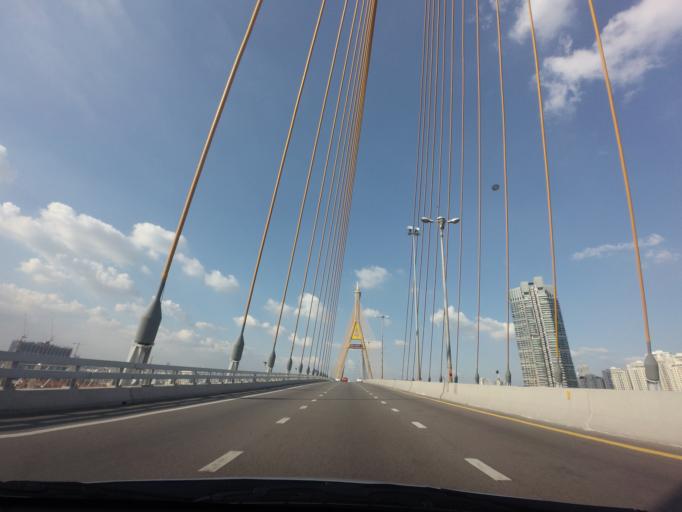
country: TH
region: Samut Prakan
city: Phra Pradaeng
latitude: 13.6678
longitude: 100.5383
